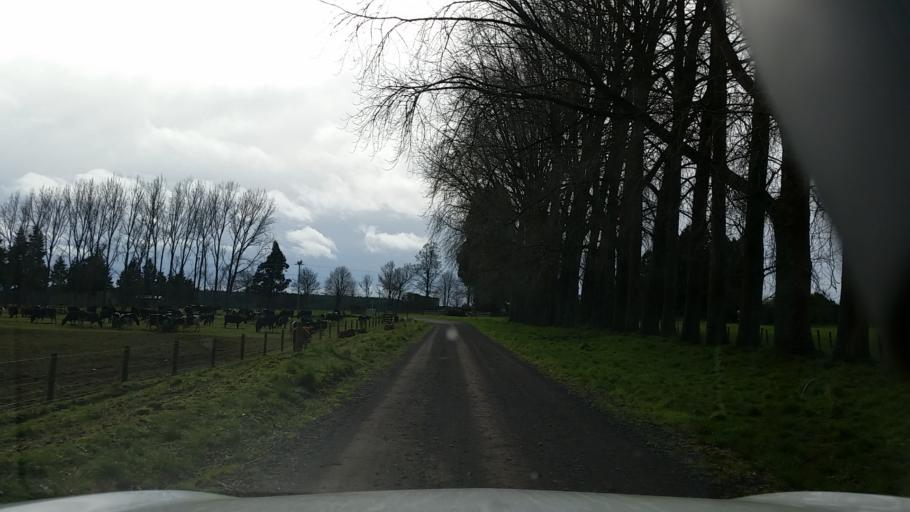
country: NZ
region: Bay of Plenty
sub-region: Whakatane District
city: Murupara
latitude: -38.4694
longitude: 176.4173
